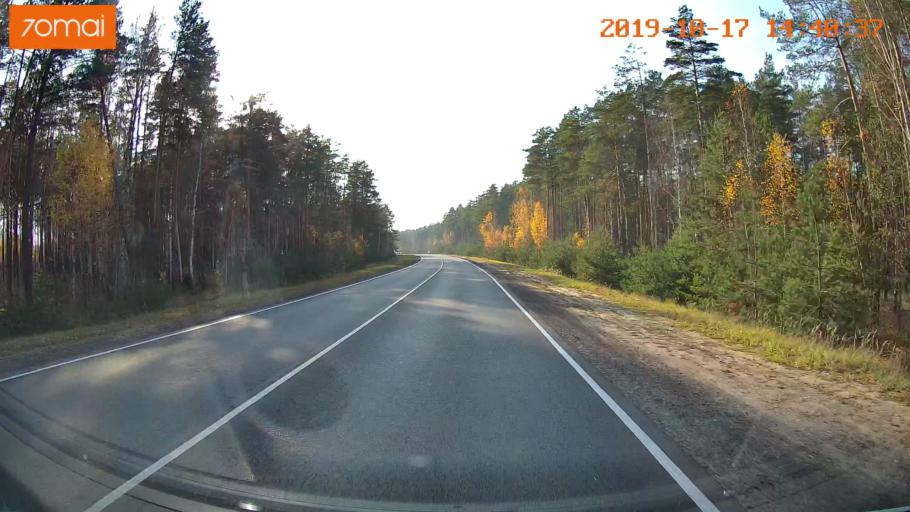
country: RU
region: Rjazan
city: Solotcha
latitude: 54.8539
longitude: 39.9534
